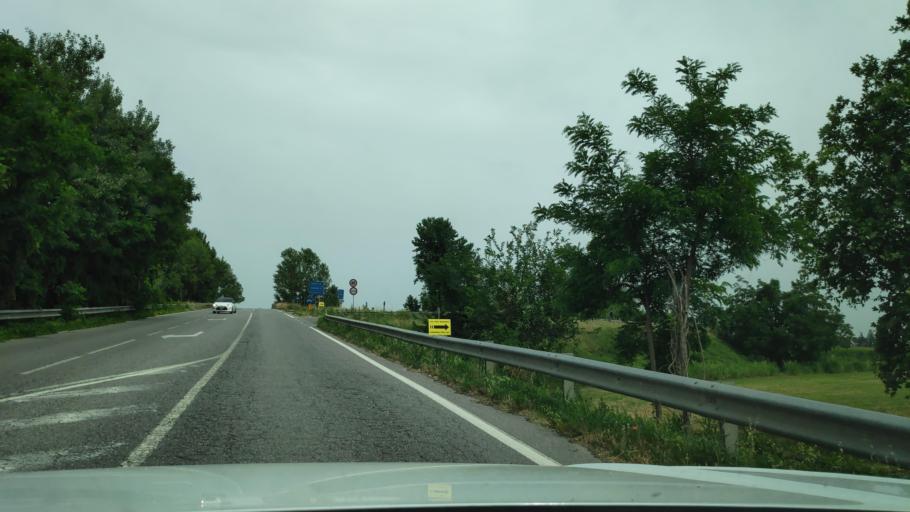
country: IT
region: Lombardy
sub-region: Provincia di Cremona
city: Soncino
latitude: 45.3998
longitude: 9.8547
